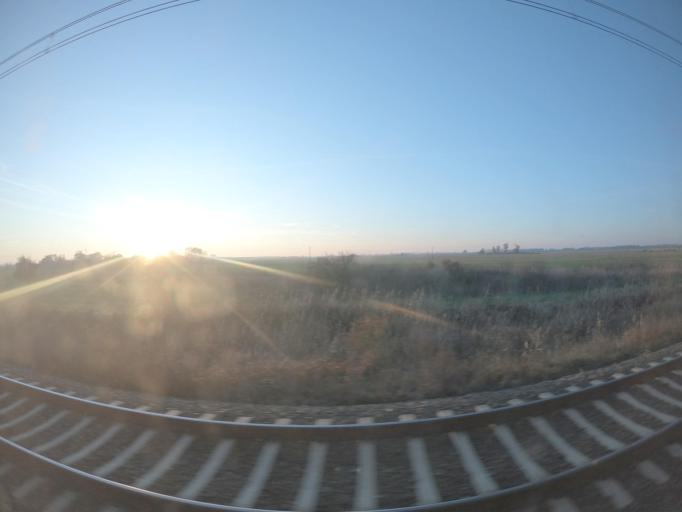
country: PL
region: Lubusz
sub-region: Powiat gorzowski
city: Kostrzyn nad Odra
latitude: 52.5452
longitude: 14.6510
